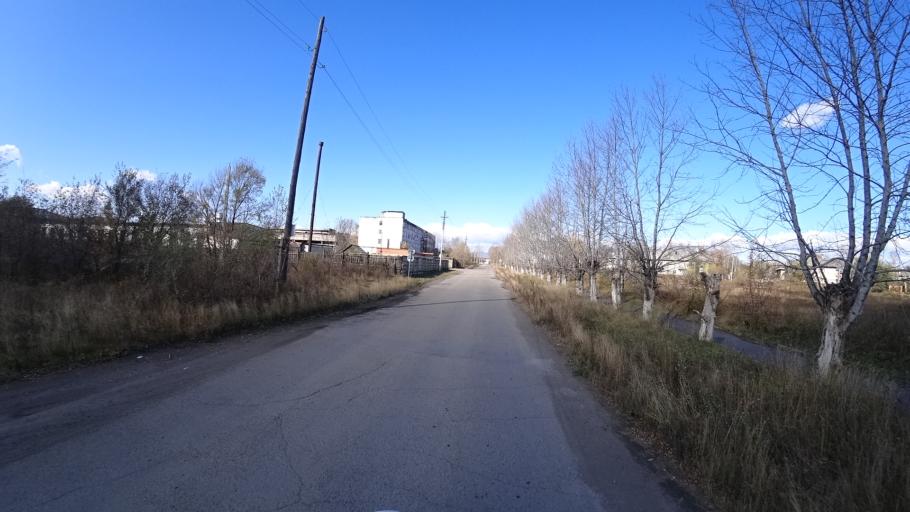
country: RU
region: Khabarovsk Krai
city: Amursk
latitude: 50.0967
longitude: 136.4958
